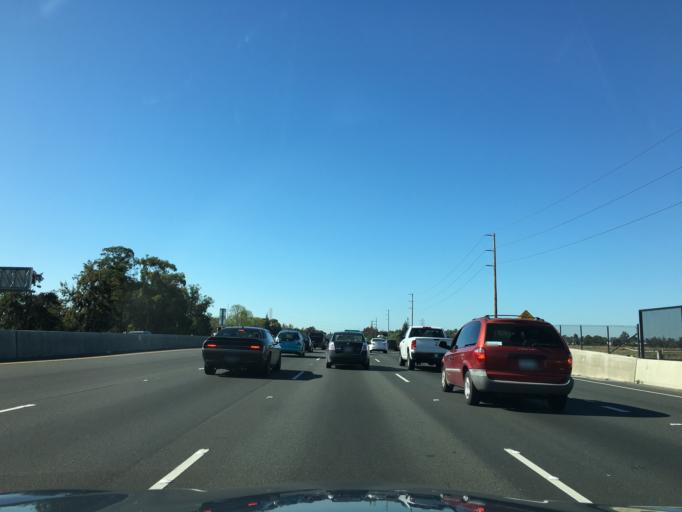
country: US
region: California
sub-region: Santa Clara County
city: Palo Alto
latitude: 37.4400
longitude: -122.1136
